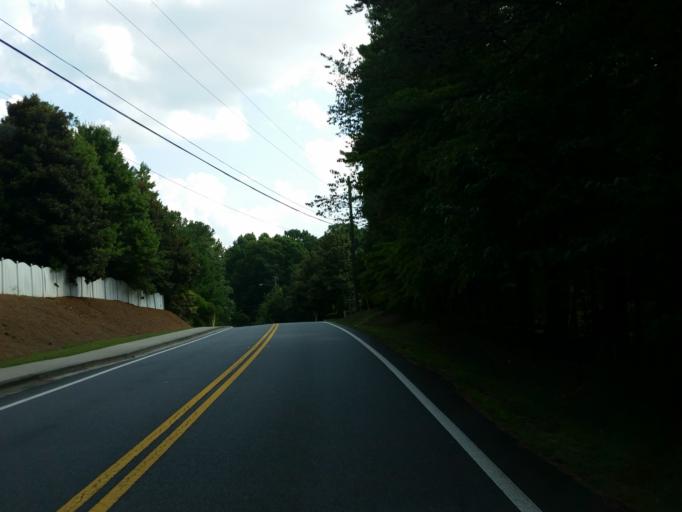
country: US
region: Georgia
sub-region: Fulton County
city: Roswell
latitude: 34.0316
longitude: -84.4423
